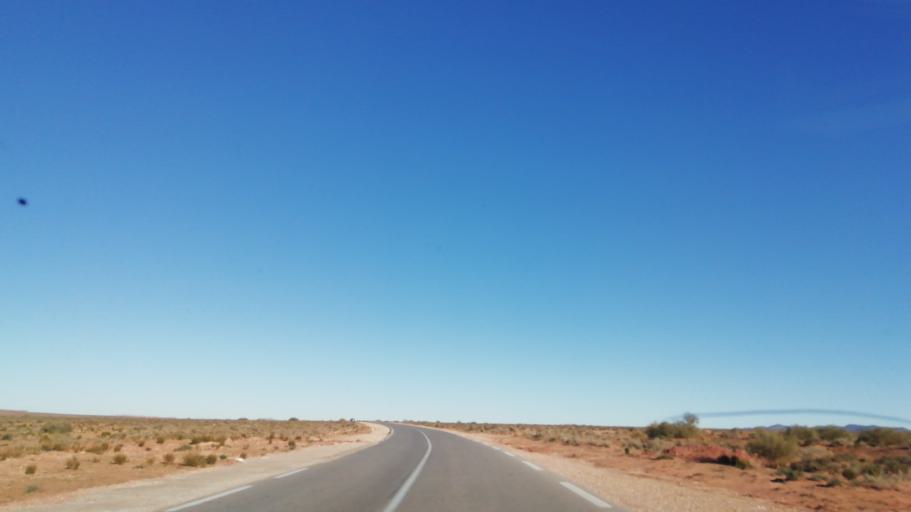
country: DZ
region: El Bayadh
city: El Abiodh Sidi Cheikh
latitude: 33.1118
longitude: 0.2585
